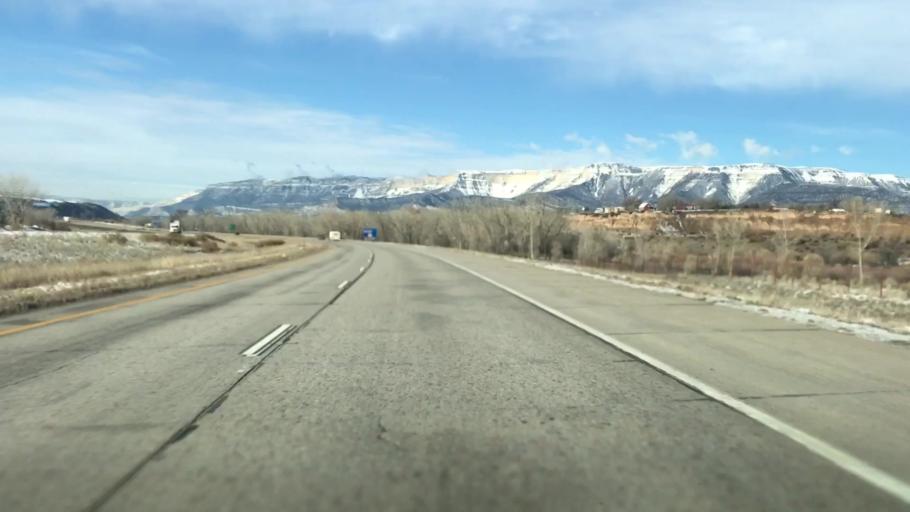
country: US
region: Colorado
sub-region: Garfield County
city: Rifle
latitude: 39.5264
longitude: -107.7655
